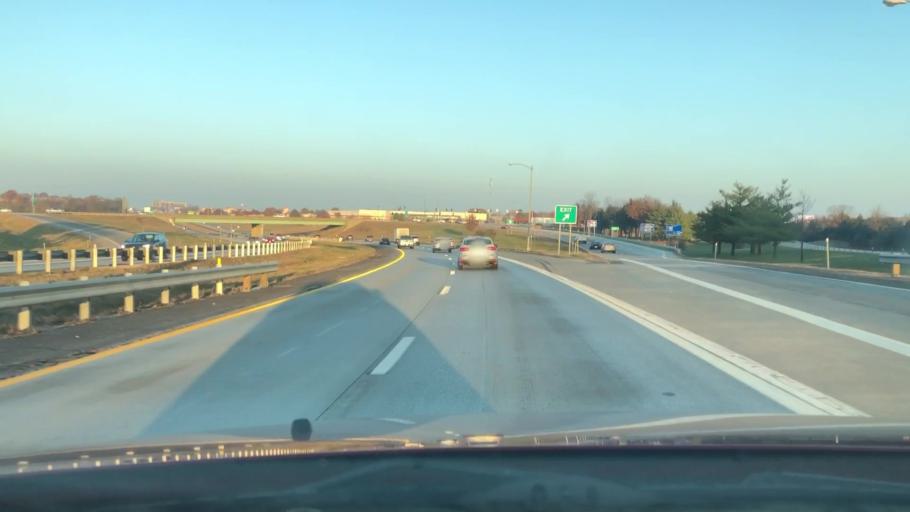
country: US
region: Missouri
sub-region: Greene County
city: Springfield
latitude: 37.1379
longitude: -93.2495
